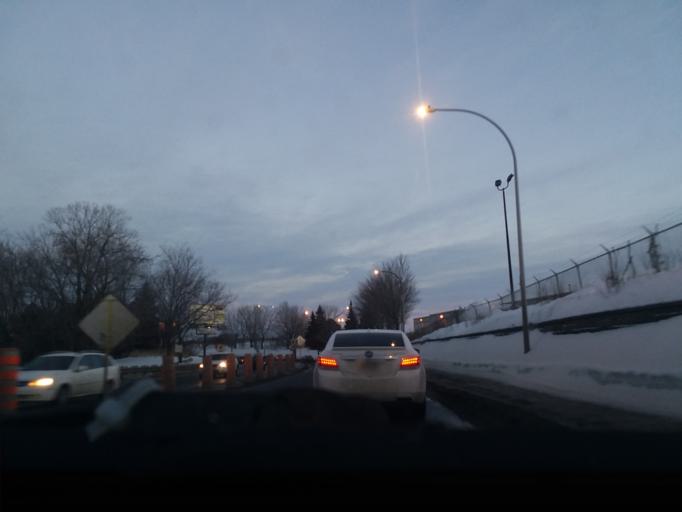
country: CA
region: Quebec
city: Saint-Raymond
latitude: 45.4504
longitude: -73.6235
